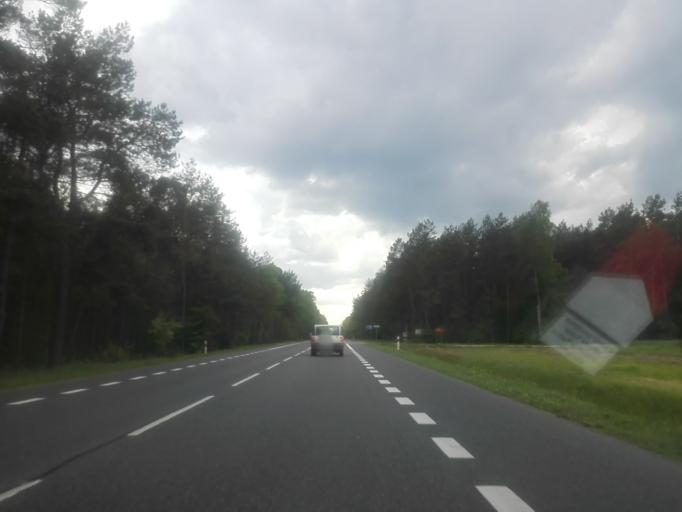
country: PL
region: Masovian Voivodeship
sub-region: Powiat ostrowski
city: Ostrow Mazowiecka
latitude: 52.8524
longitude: 21.9857
